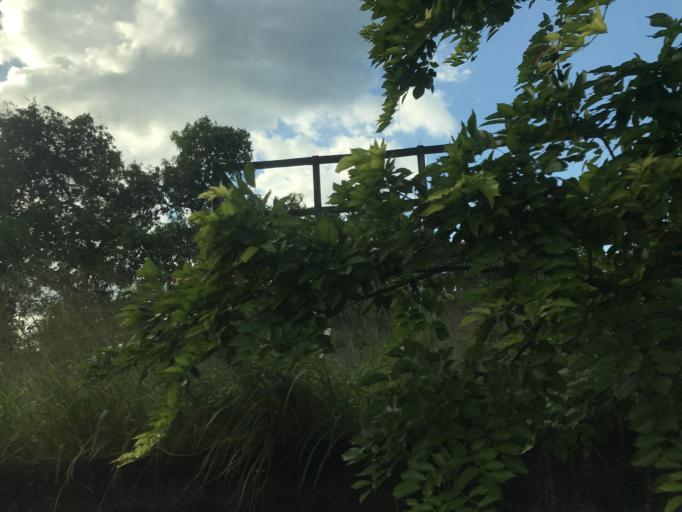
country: LK
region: Western
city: Gampaha
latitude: 7.0899
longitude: 79.9911
